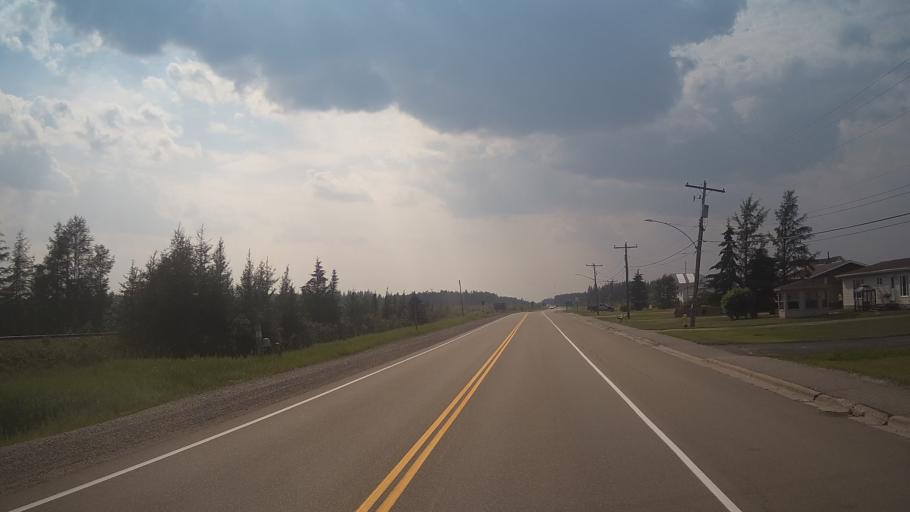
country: CA
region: Ontario
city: Kapuskasing
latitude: 49.5279
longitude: -82.8724
